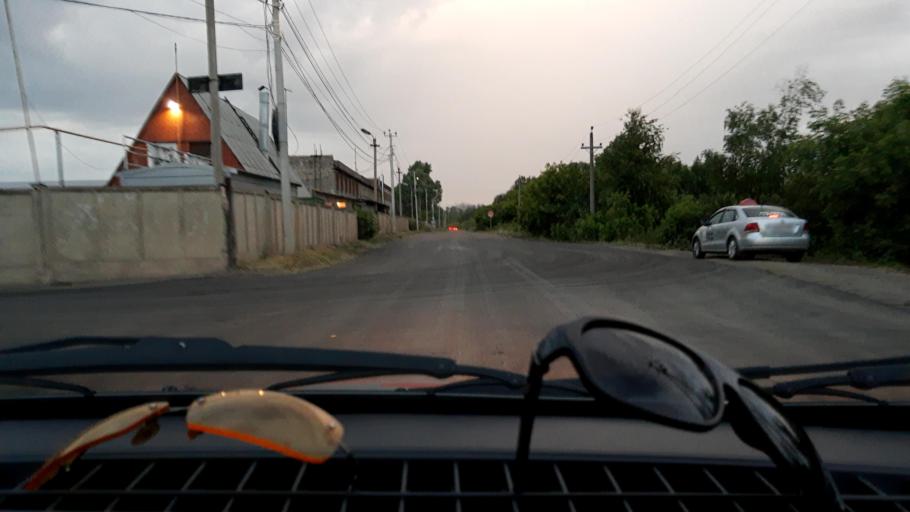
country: RU
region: Bashkortostan
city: Avdon
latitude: 54.6668
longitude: 55.8239
